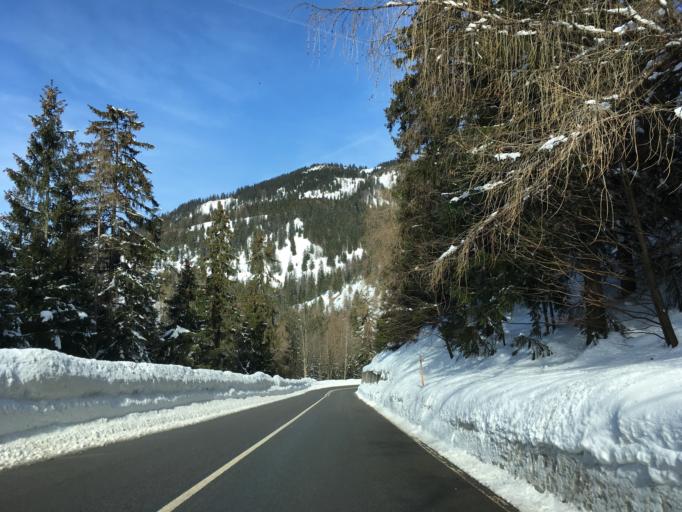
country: DE
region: Bavaria
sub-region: Upper Bavaria
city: Bayrischzell
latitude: 47.6804
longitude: 12.0144
